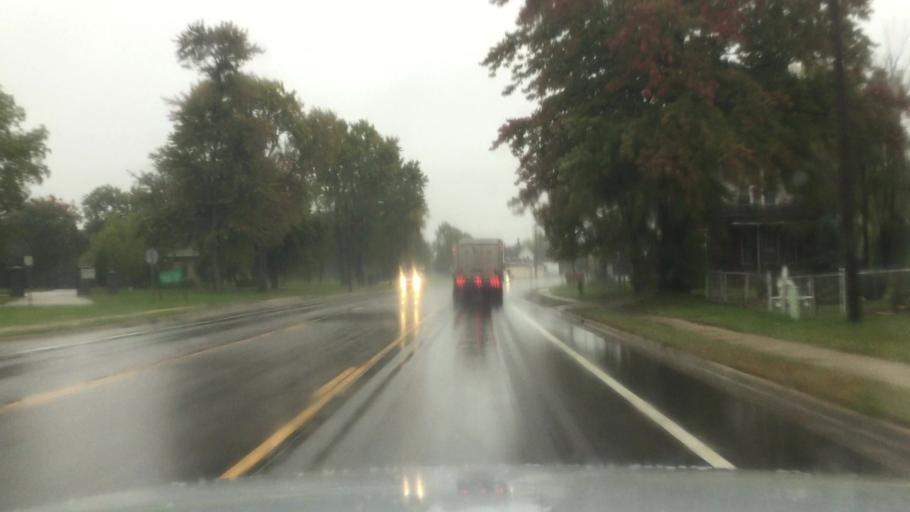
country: US
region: Michigan
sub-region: Saginaw County
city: Saginaw
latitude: 43.3970
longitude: -83.9565
